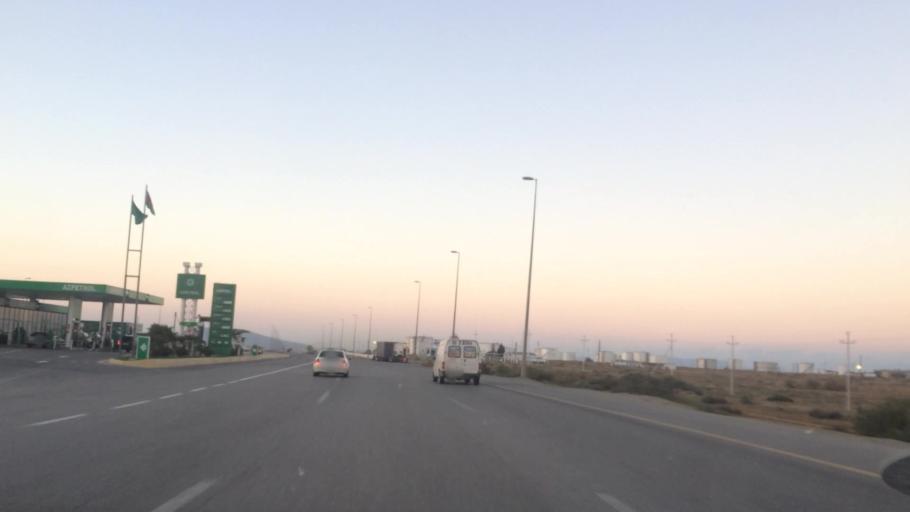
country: AZ
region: Baki
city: Qobustan
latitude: 39.9938
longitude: 49.4315
